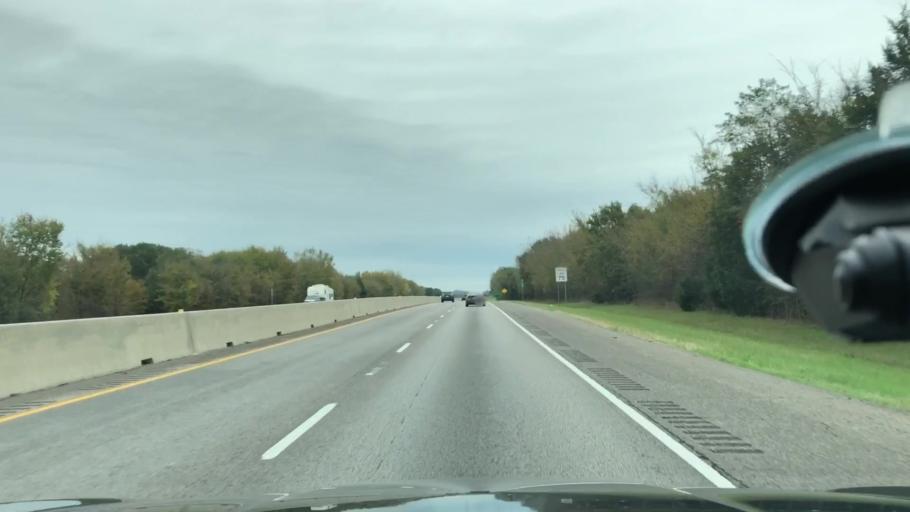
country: US
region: Texas
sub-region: Franklin County
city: Mount Vernon
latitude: 33.1667
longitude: -95.3187
